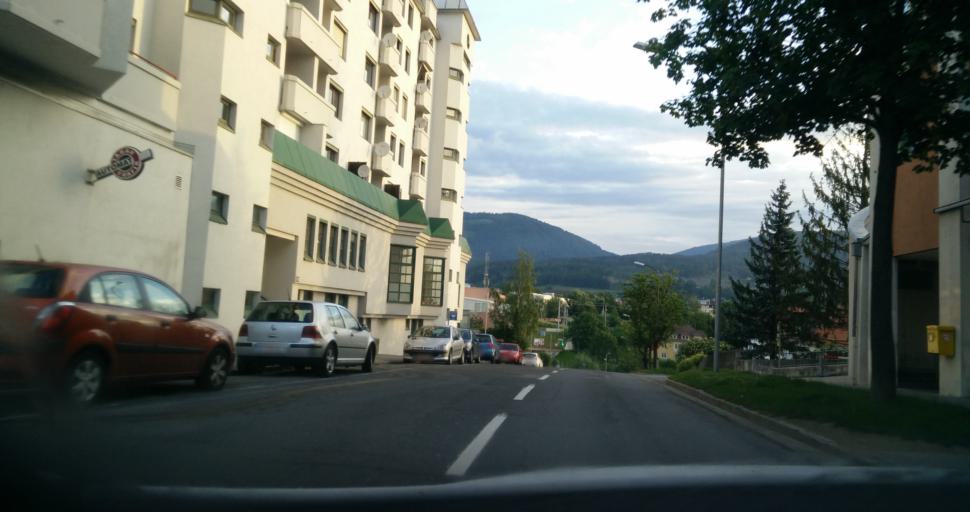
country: AT
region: Carinthia
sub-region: Villach Stadt
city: Villach
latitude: 46.6145
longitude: 13.8430
